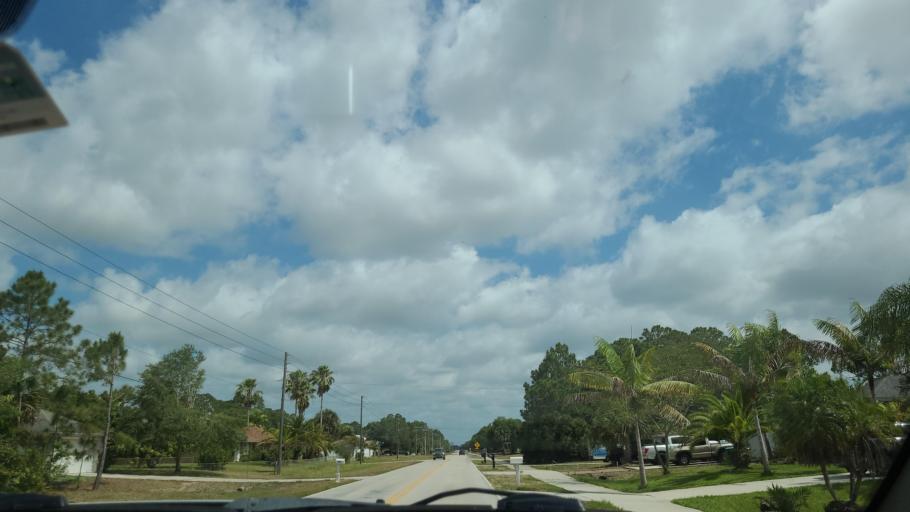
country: US
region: Florida
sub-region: Brevard County
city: June Park
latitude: 28.0027
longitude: -80.6969
